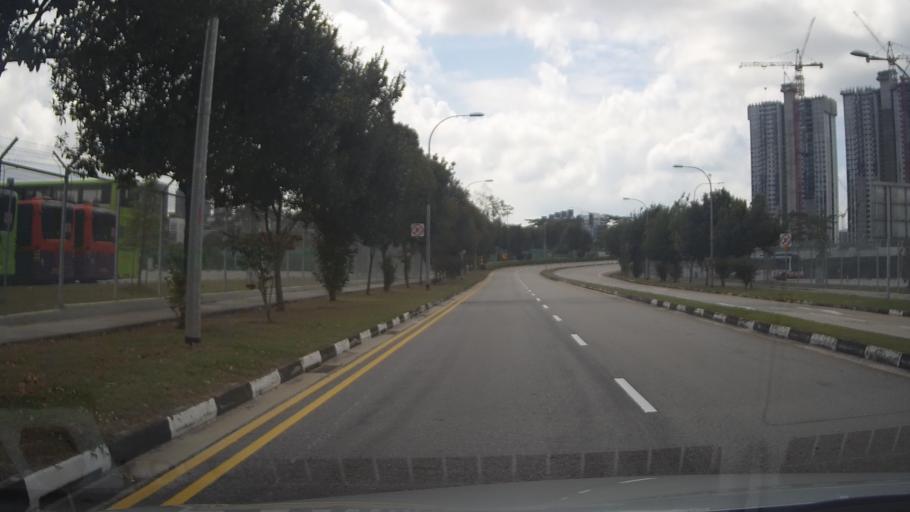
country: SG
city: Singapore
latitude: 1.3263
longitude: 103.7537
